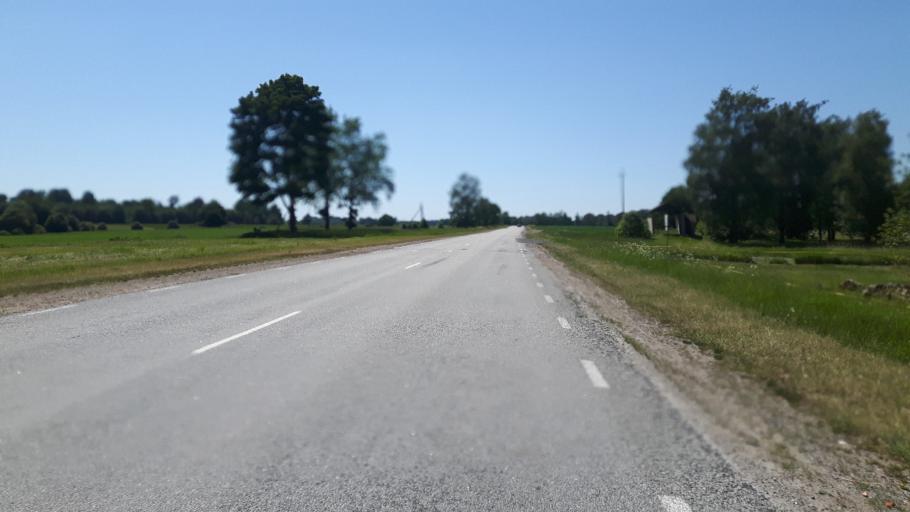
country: EE
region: Paernumaa
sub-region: Sindi linn
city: Sindi
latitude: 58.4471
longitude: 24.7662
